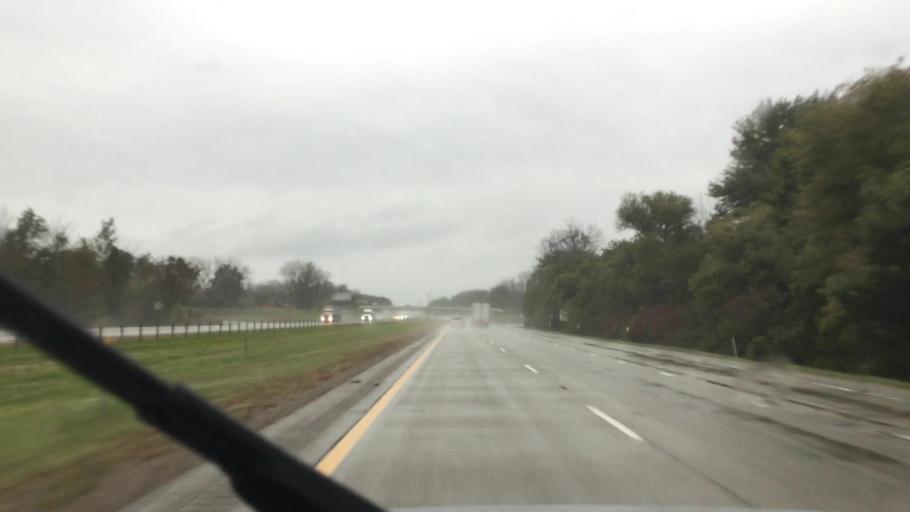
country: US
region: Michigan
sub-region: Van Buren County
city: Hartford
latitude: 42.1930
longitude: -86.1602
